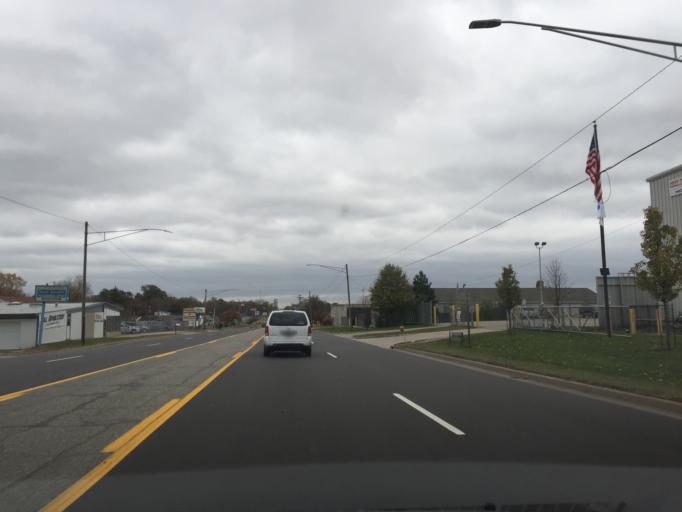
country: US
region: Michigan
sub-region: Oakland County
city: Pontiac
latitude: 42.6581
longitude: -83.3182
